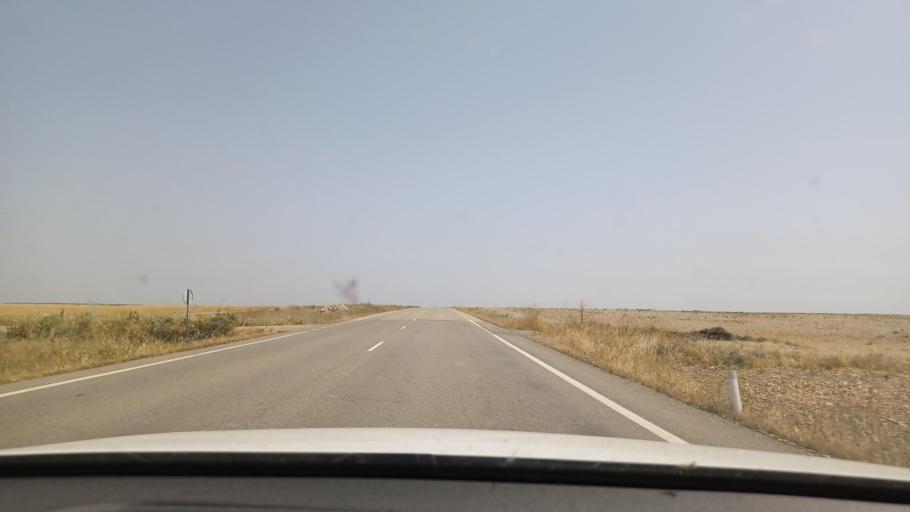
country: ES
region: Aragon
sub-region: Provincia de Zaragoza
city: Bujaraloz
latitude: 41.4088
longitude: -0.1225
